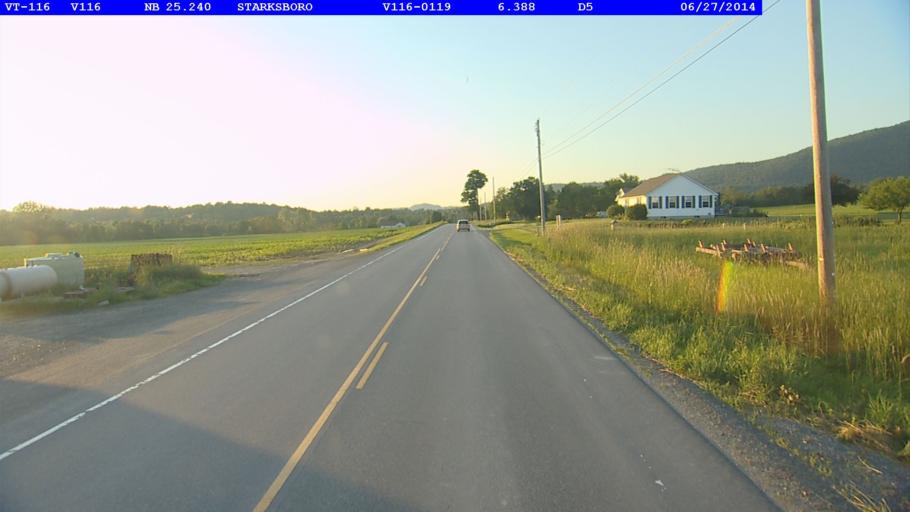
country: US
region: Vermont
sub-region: Chittenden County
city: Hinesburg
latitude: 44.2760
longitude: -73.0675
